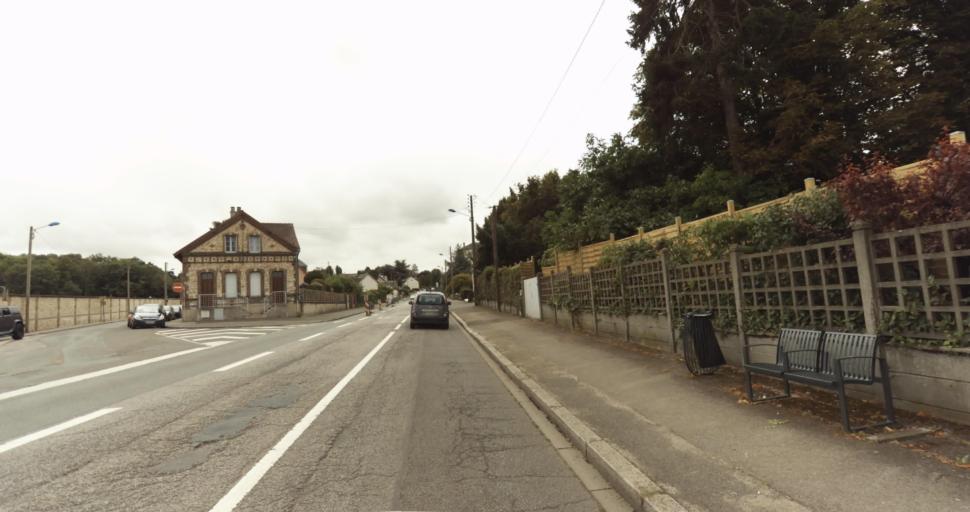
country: FR
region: Haute-Normandie
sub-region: Departement de l'Eure
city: Evreux
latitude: 49.0231
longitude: 1.1555
